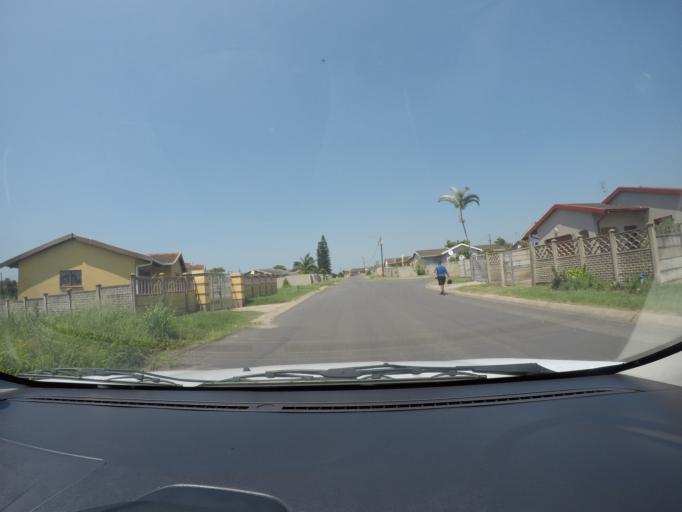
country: ZA
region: KwaZulu-Natal
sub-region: uThungulu District Municipality
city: eSikhawini
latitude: -28.8657
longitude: 31.9209
